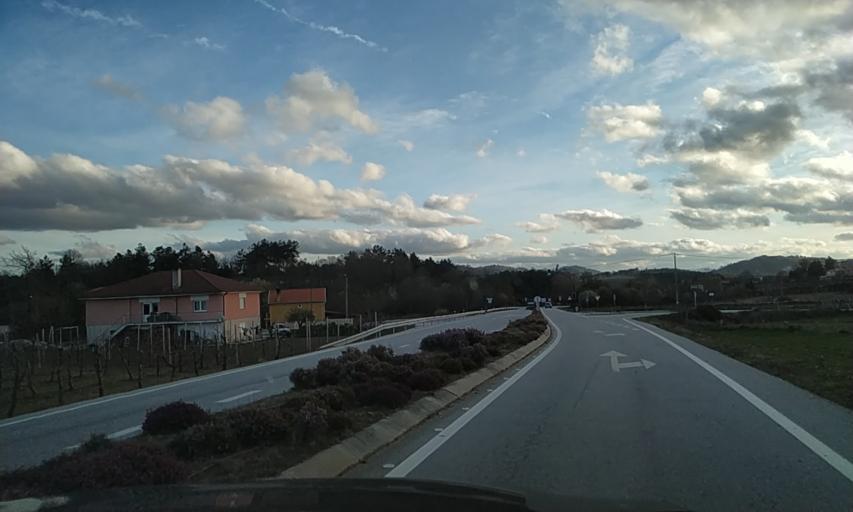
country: PT
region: Braganca
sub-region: Carrazeda de Ansiaes
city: Carrazeda de Anciaes
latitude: 41.2361
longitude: -7.3247
